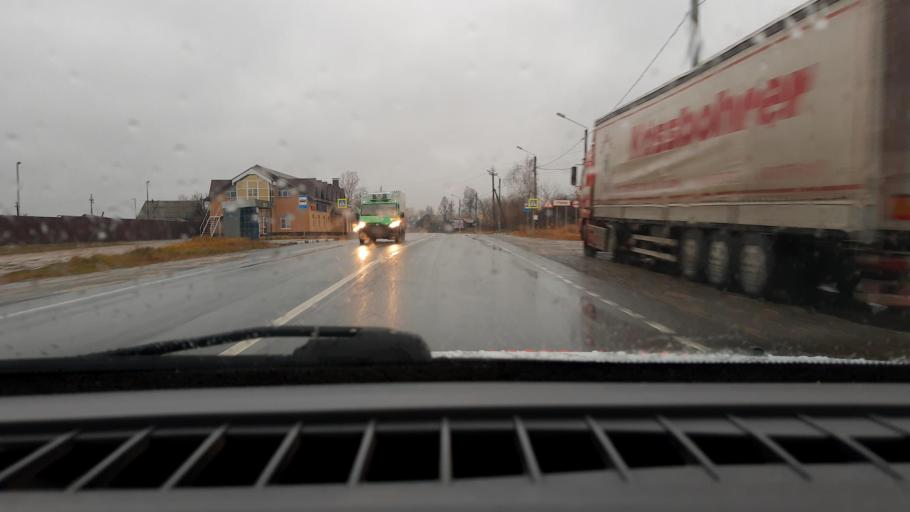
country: RU
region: Nizjnij Novgorod
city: Sitniki
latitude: 56.5423
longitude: 44.0195
